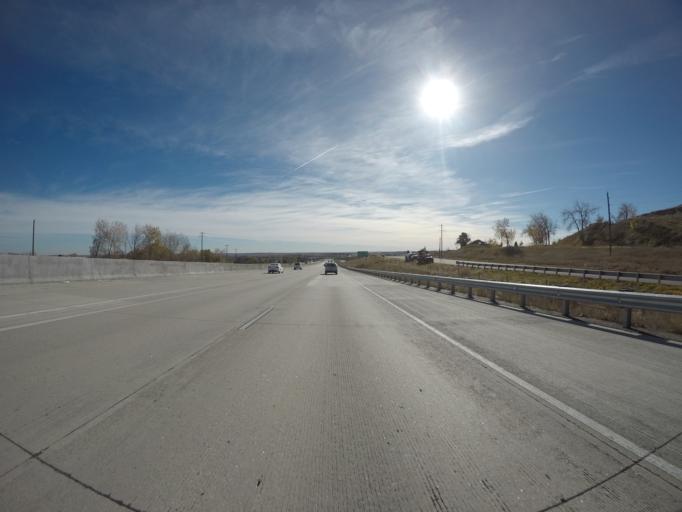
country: US
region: Colorado
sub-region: Boulder County
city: Superior
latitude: 39.9636
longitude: -105.1810
